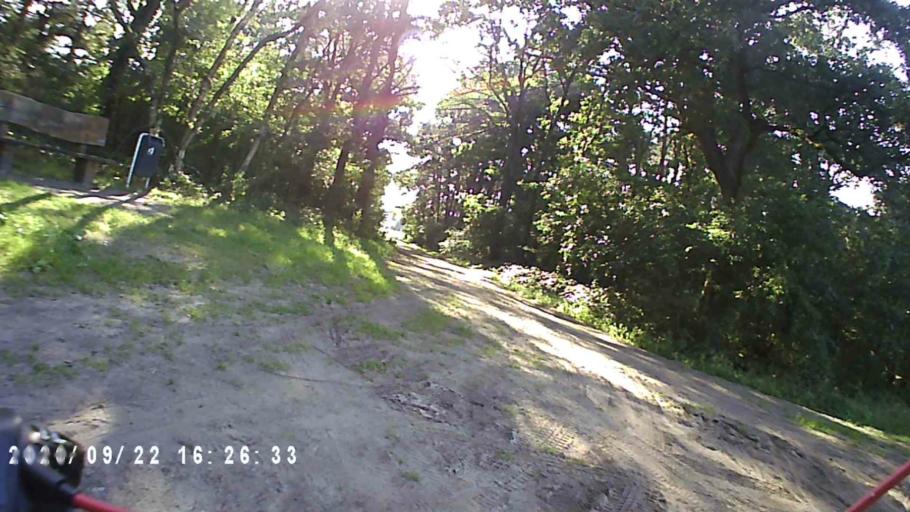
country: NL
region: Groningen
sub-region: Gemeente Leek
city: Leek
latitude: 53.0782
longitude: 6.4340
